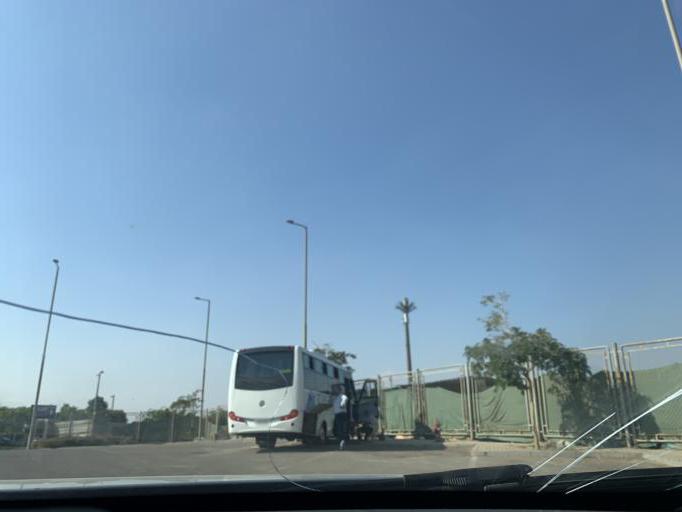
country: EG
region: Muhafazat al Qahirah
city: Cairo
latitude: 30.0324
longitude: 31.4053
